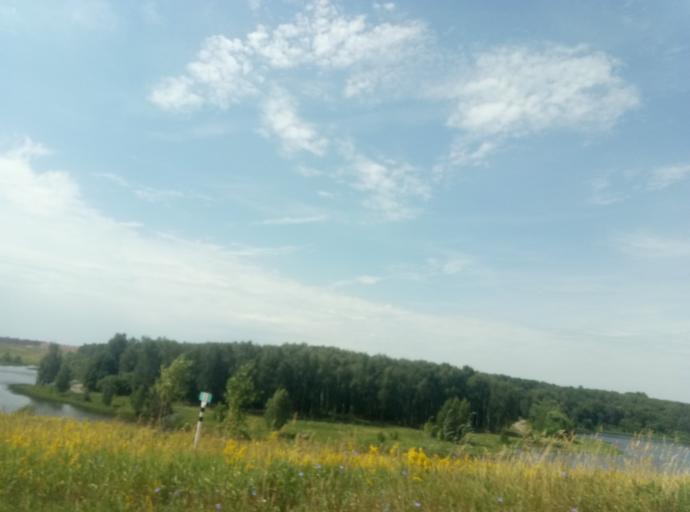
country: RU
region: Tula
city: Kireyevsk
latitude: 53.9314
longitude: 37.9499
